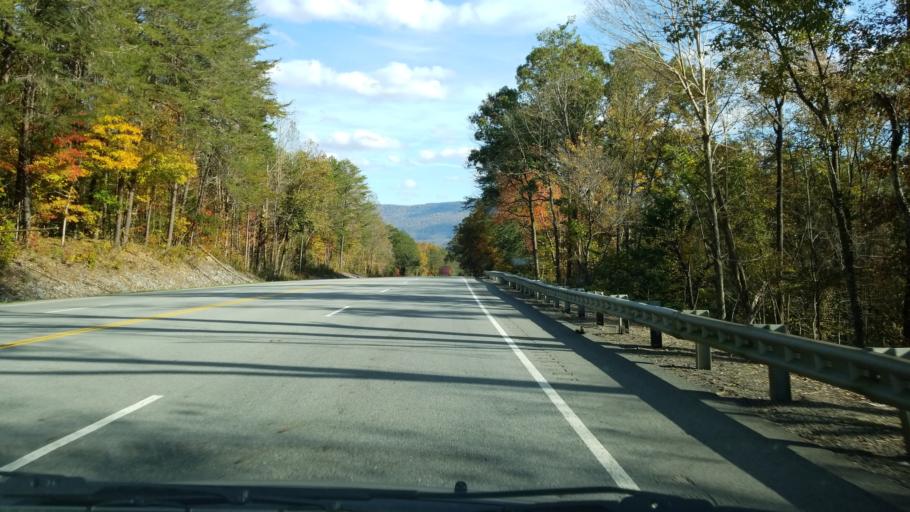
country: US
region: Tennessee
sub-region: Sequatchie County
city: Dunlap
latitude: 35.4060
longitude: -85.3961
